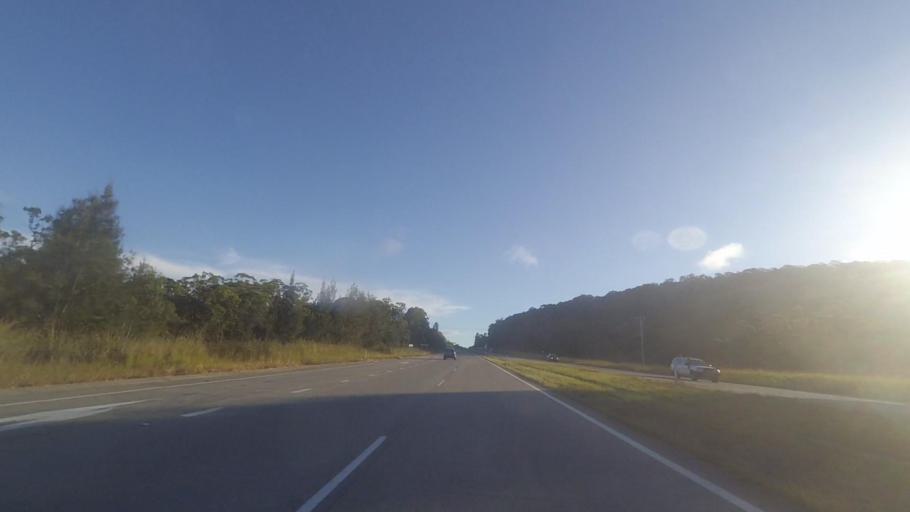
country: AU
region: New South Wales
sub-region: Great Lakes
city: Bulahdelah
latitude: -32.4672
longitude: 152.1962
